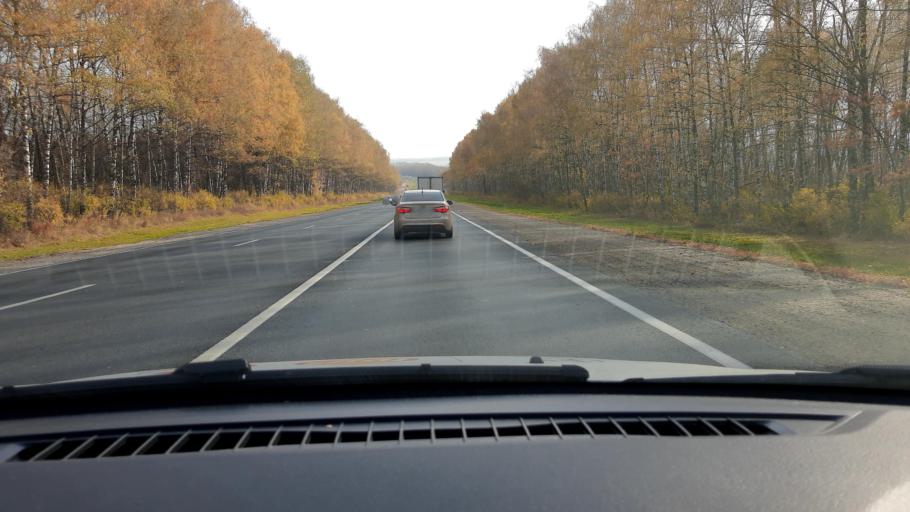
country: RU
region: Nizjnij Novgorod
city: Pamyat' Parizhskoy Kommuny
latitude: 56.0526
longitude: 44.4079
